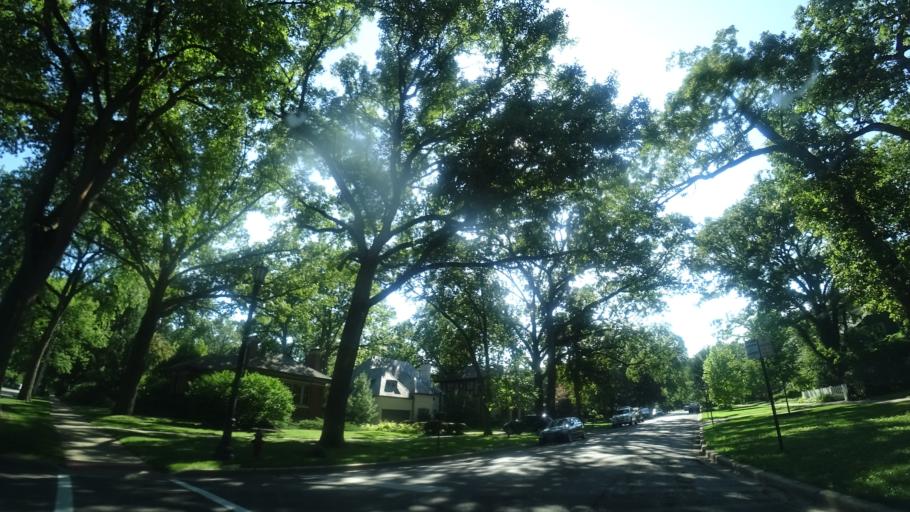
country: US
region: Illinois
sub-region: Cook County
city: Wilmette
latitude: 42.0624
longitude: -87.7034
